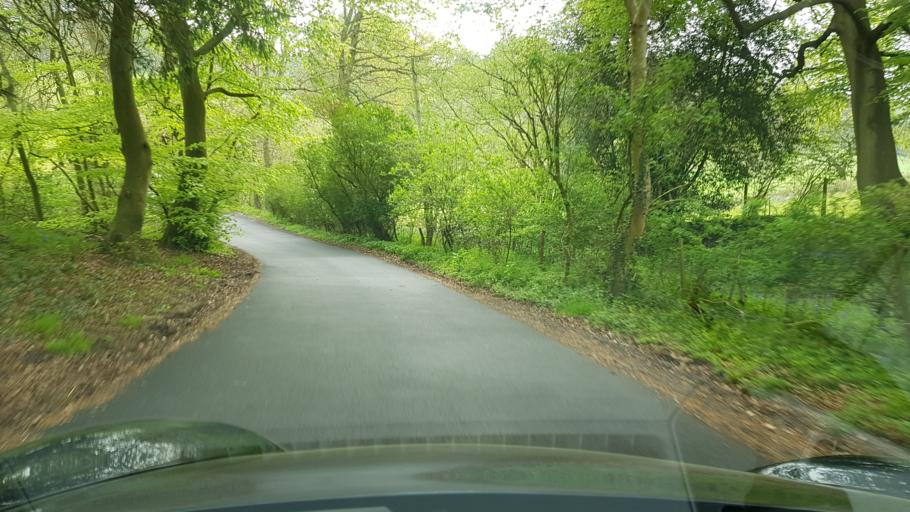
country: GB
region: England
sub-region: Surrey
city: East Horsley
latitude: 51.2457
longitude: -0.4470
